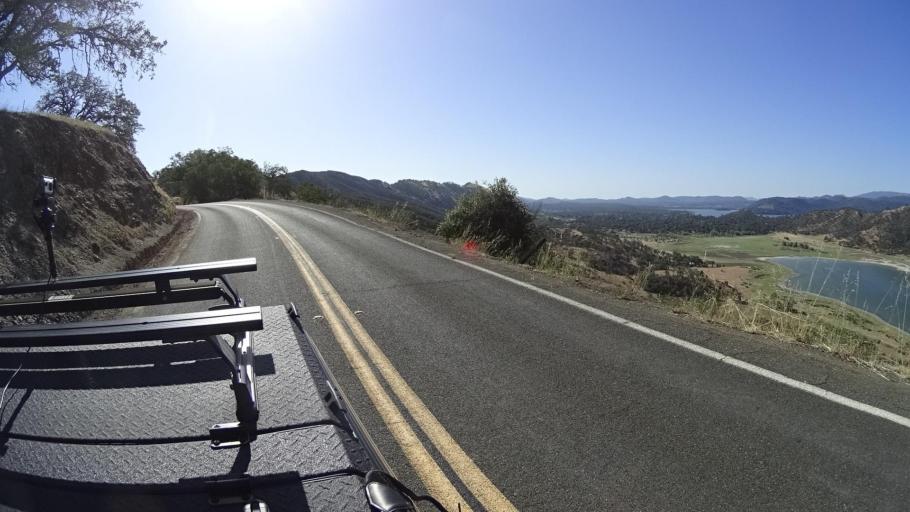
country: US
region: California
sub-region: Lake County
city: Clearlake Oaks
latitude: 38.9945
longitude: -122.6740
